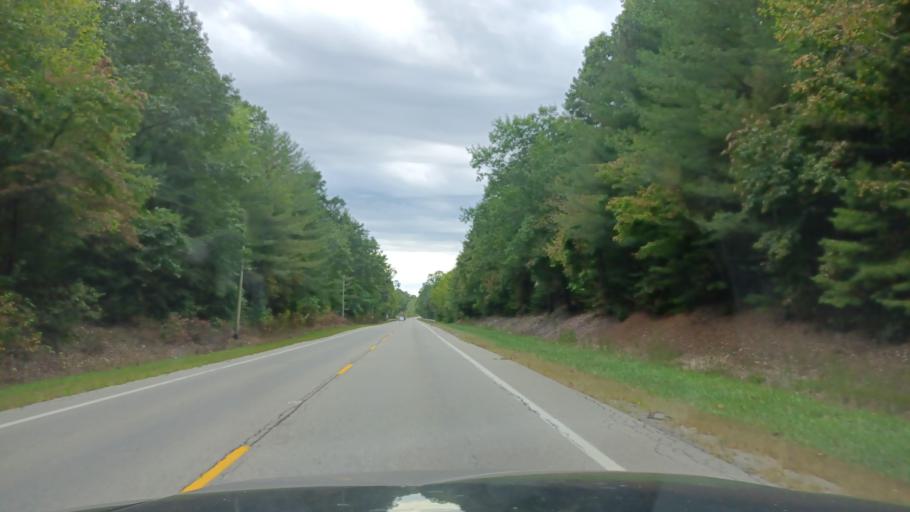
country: US
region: Ohio
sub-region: Vinton County
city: McArthur
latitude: 39.2367
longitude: -82.4112
